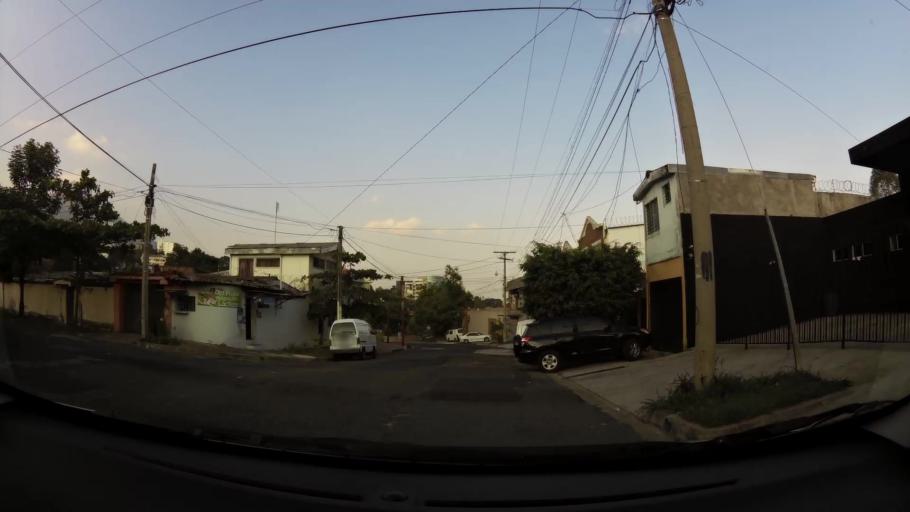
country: SV
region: La Libertad
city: Antiguo Cuscatlan
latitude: 13.7007
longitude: -89.2470
